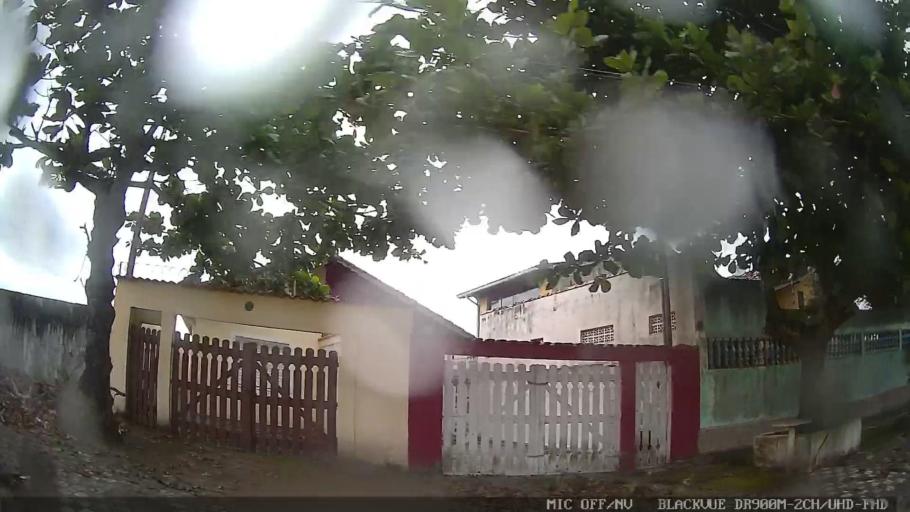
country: BR
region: Sao Paulo
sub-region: Mongagua
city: Mongagua
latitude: -24.1351
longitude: -46.6990
